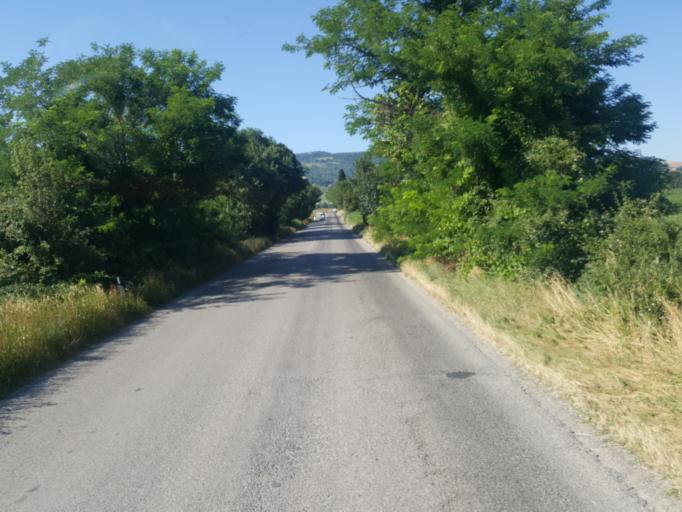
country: IT
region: The Marches
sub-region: Provincia di Pesaro e Urbino
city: Padiglione
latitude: 43.8445
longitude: 12.7202
